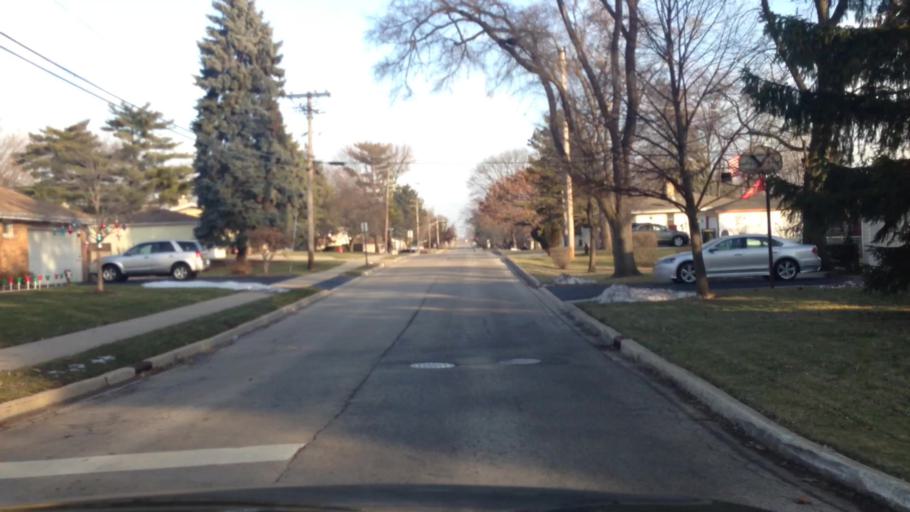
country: US
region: Illinois
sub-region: DuPage County
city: Wood Dale
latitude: 41.9669
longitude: -87.9773
